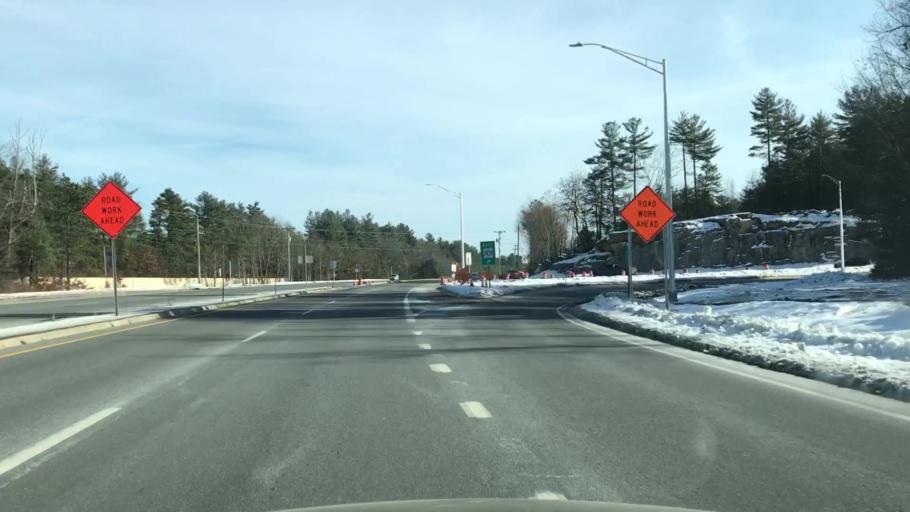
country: US
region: New Hampshire
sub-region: Hillsborough County
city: Milford
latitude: 42.8247
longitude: -71.6162
